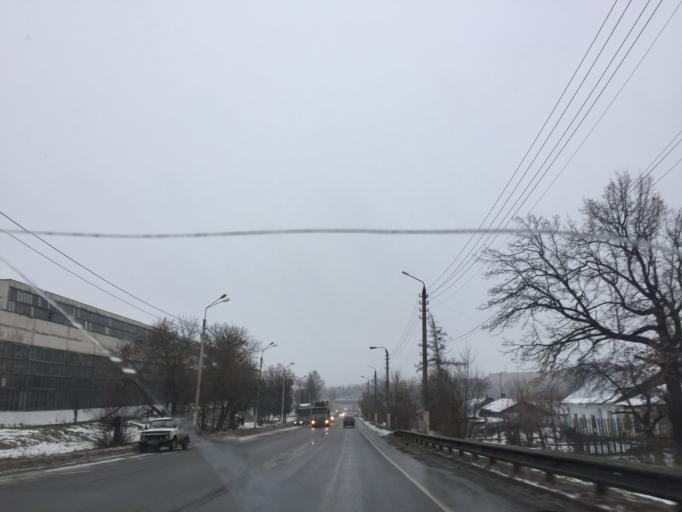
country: RU
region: Tula
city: Plavsk
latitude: 53.7158
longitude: 37.2971
